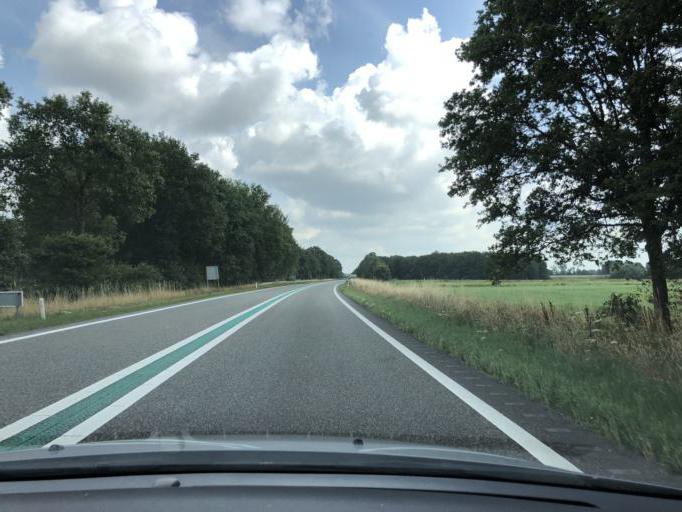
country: NL
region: Drenthe
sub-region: Gemeente Hoogeveen
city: Hoogeveen
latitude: 52.6184
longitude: 6.4124
